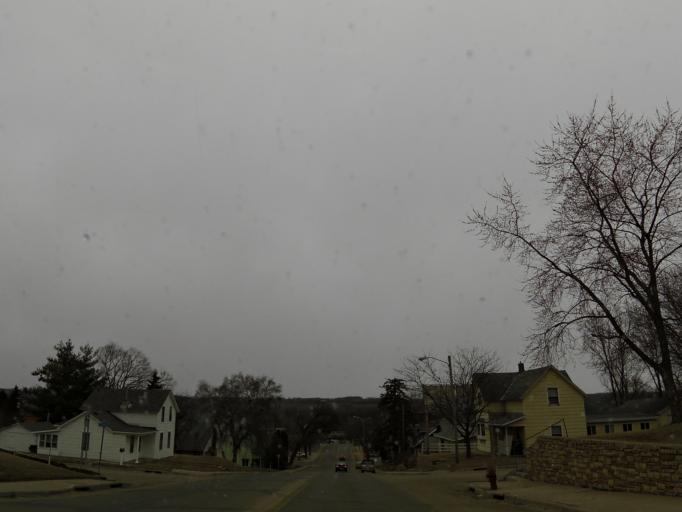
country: US
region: Minnesota
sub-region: Le Sueur County
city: Le Sueur
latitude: 44.4602
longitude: -93.9126
